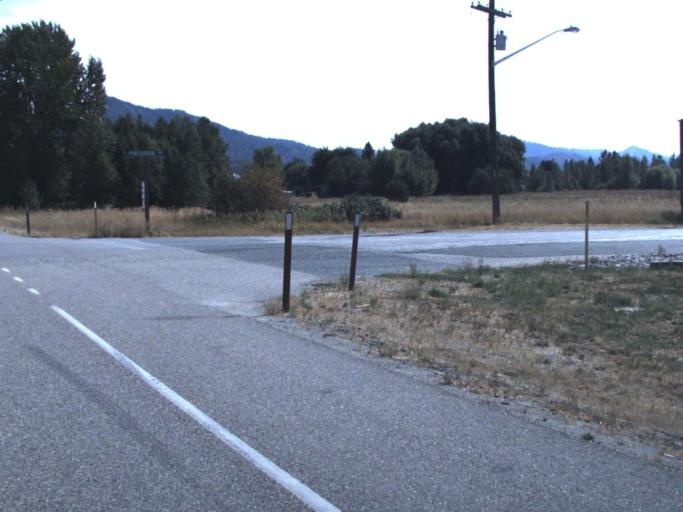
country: US
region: Washington
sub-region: Stevens County
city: Chewelah
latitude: 48.2884
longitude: -117.7266
